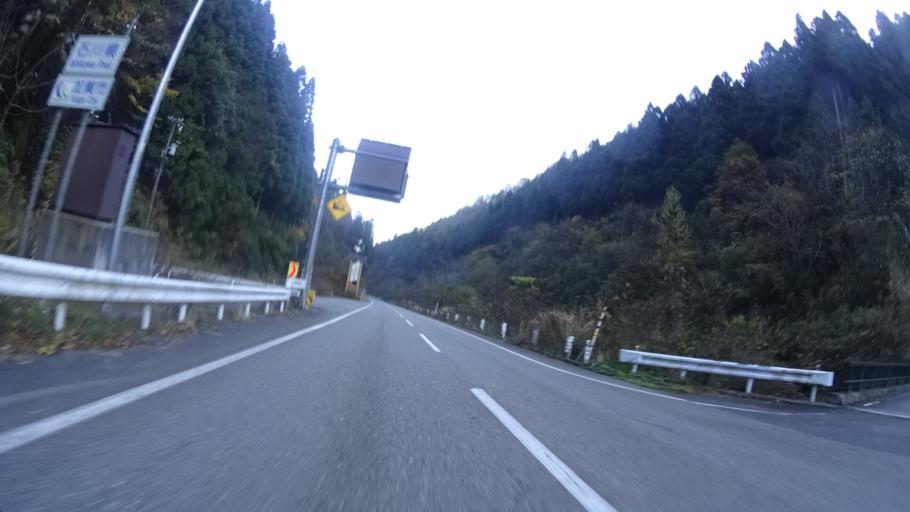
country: JP
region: Fukui
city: Maruoka
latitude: 36.1870
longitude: 136.3424
